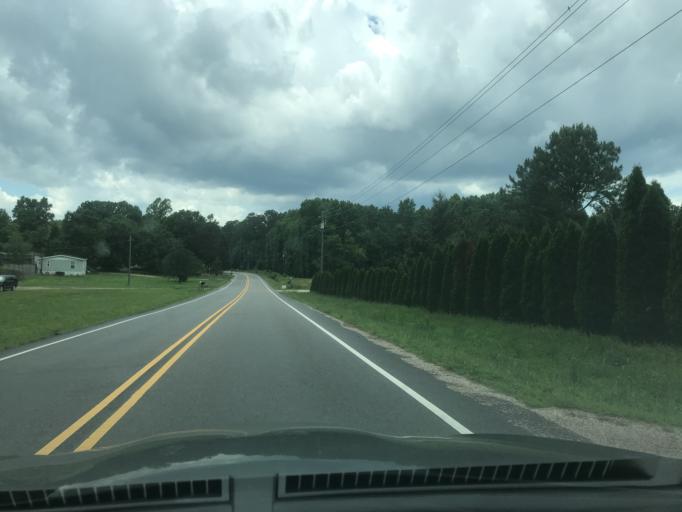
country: US
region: North Carolina
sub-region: Wake County
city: Knightdale
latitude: 35.8355
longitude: -78.4746
